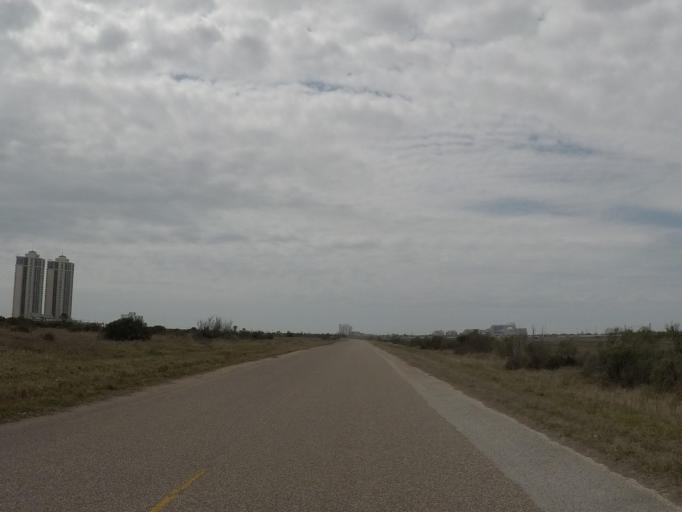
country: US
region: Texas
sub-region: Galveston County
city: Galveston
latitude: 29.3234
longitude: -94.7513
